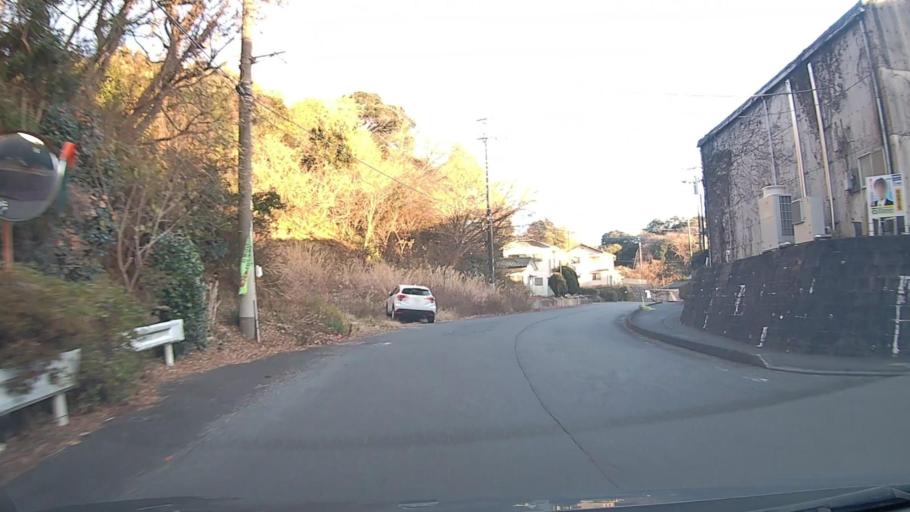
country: JP
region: Ibaraki
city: Kitaibaraki
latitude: 36.8540
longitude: 140.7861
